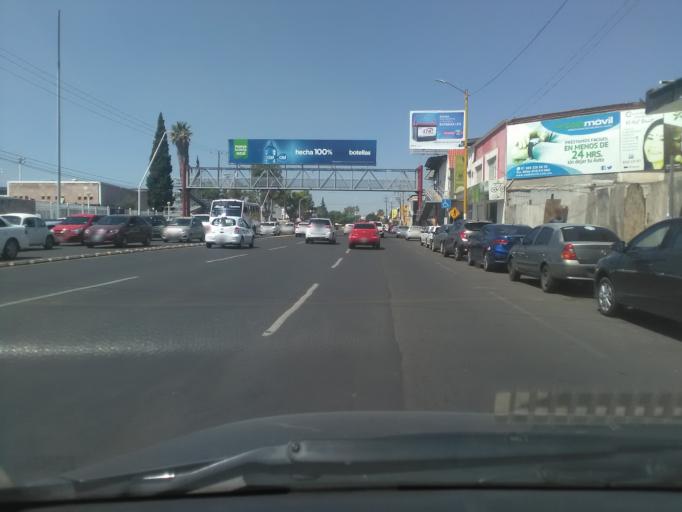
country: MX
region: Durango
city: Victoria de Durango
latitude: 24.0289
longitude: -104.6439
